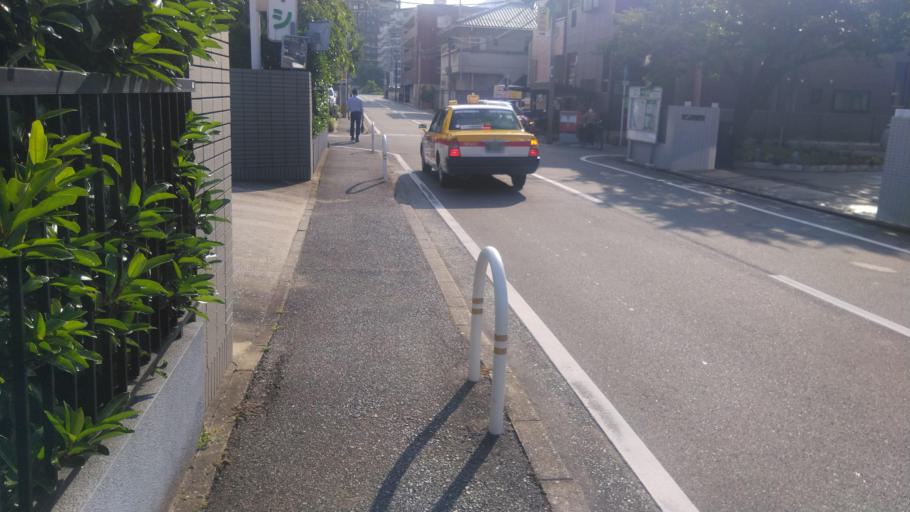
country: JP
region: Fukuoka
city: Fukuoka-shi
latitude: 33.5747
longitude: 130.4160
